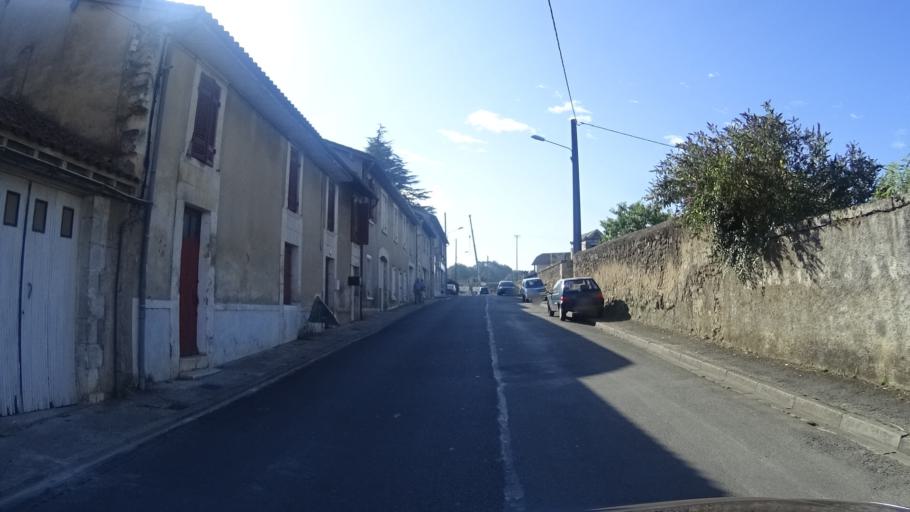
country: FR
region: Aquitaine
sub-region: Departement de la Dordogne
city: Mussidan
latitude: 45.0347
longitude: 0.3701
